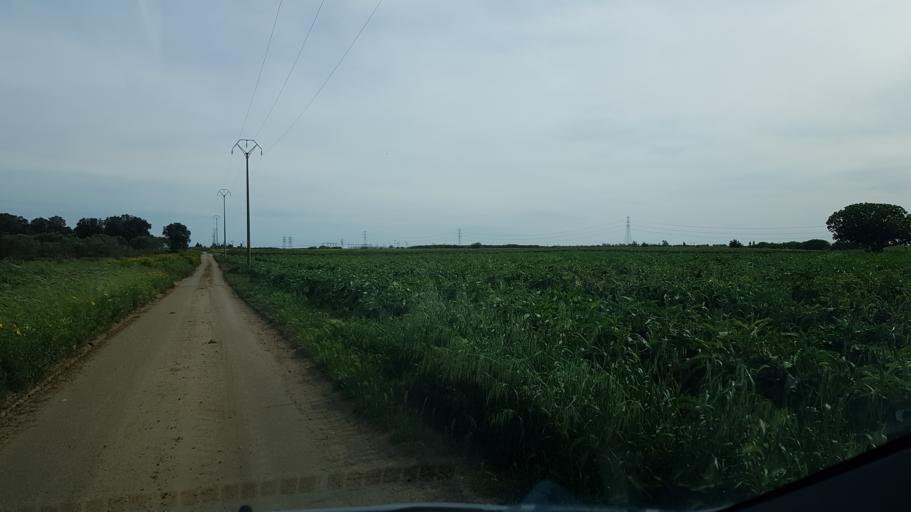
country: IT
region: Apulia
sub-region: Provincia di Brindisi
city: Tuturano
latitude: 40.5755
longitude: 17.9208
